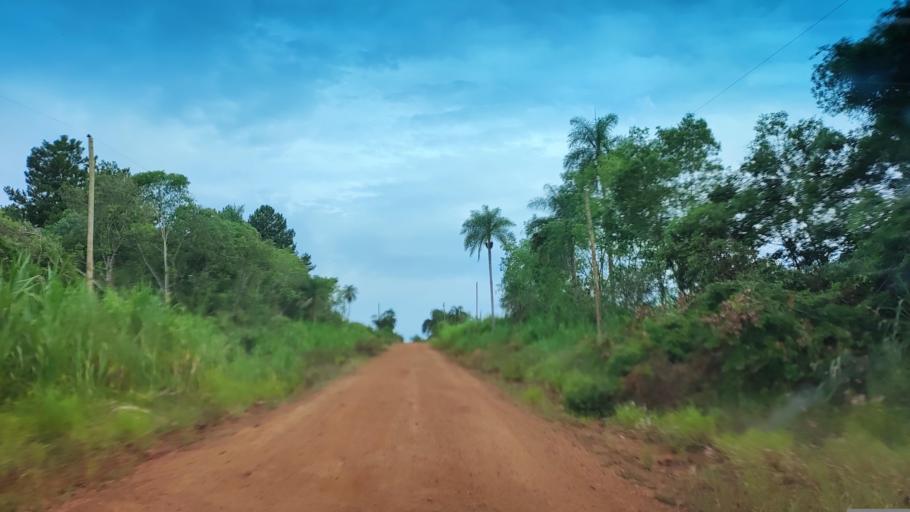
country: AR
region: Misiones
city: Gobernador Roca
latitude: -27.1597
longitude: -55.4619
